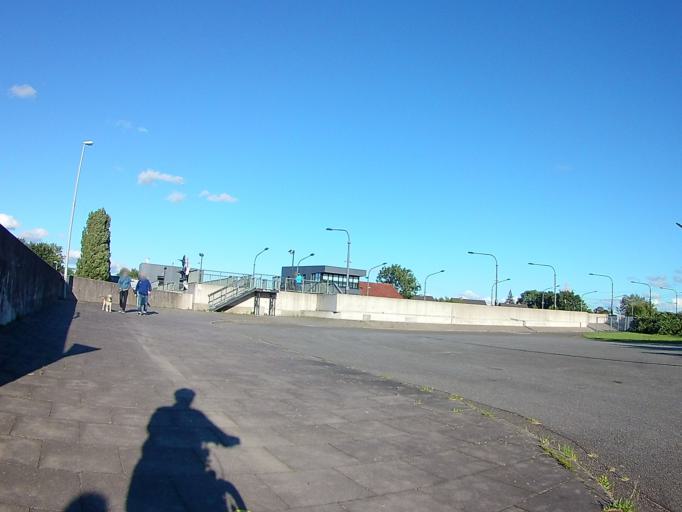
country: DE
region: Hamburg
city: Harburg
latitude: 53.4717
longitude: 9.9896
